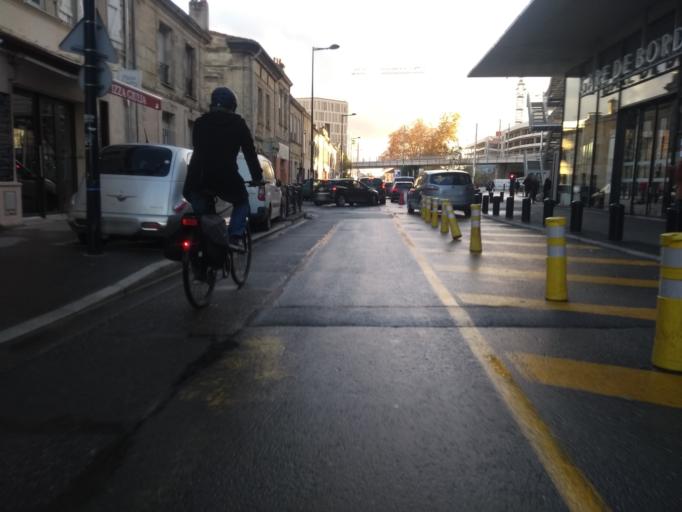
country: FR
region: Aquitaine
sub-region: Departement de la Gironde
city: Begles
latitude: 44.8244
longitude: -0.5547
